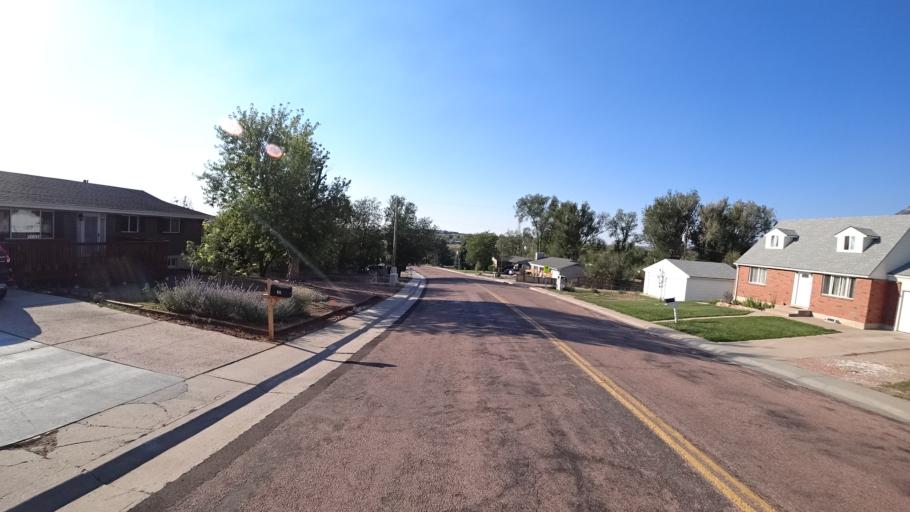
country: US
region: Colorado
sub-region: El Paso County
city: Stratmoor
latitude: 38.7774
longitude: -104.7914
